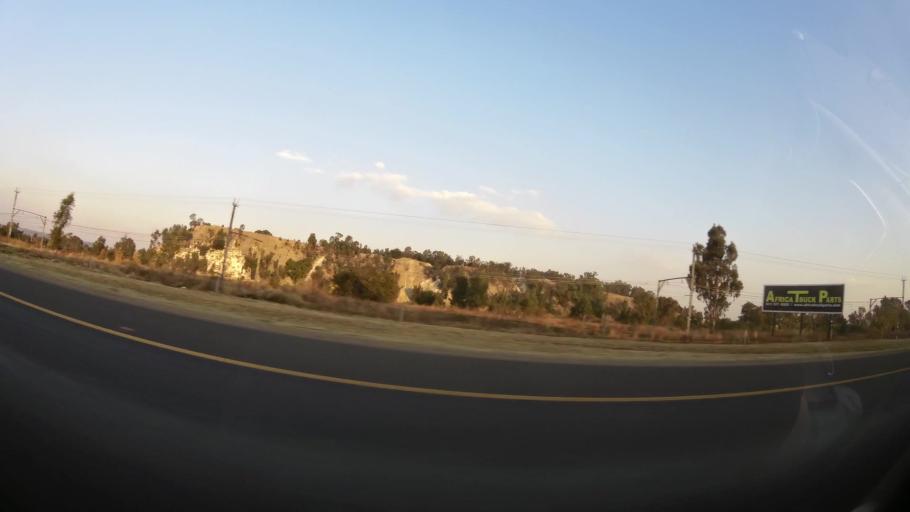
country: ZA
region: Gauteng
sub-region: Ekurhuleni Metropolitan Municipality
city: Benoni
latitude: -26.1686
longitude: 28.3531
